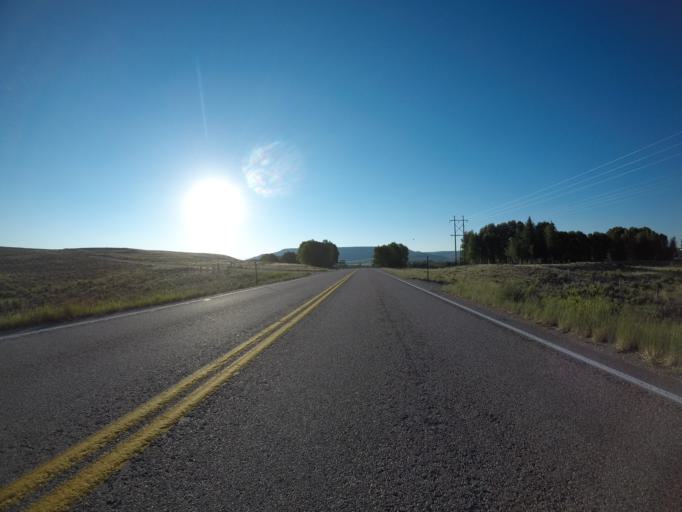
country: US
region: Wyoming
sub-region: Sublette County
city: Marbleton
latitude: 42.5699
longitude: -109.9584
